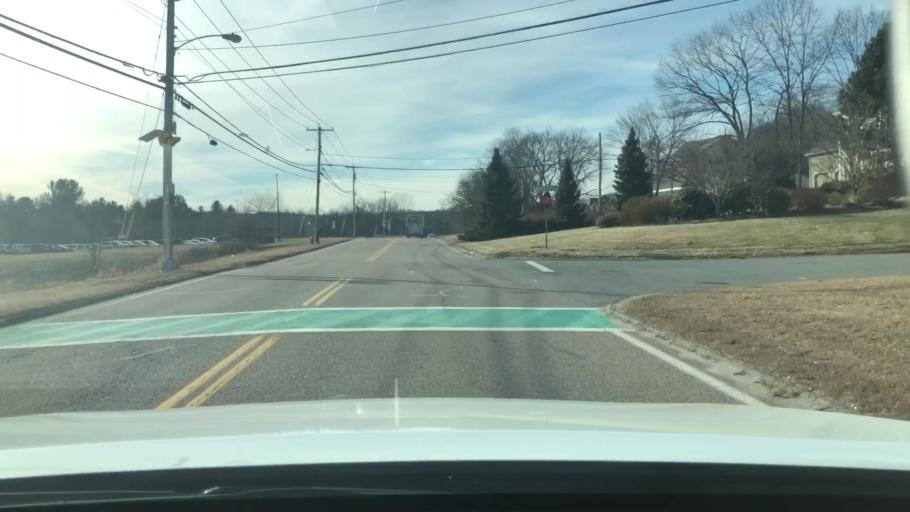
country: US
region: Massachusetts
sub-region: Worcester County
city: Grafton
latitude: 42.1994
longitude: -71.7104
